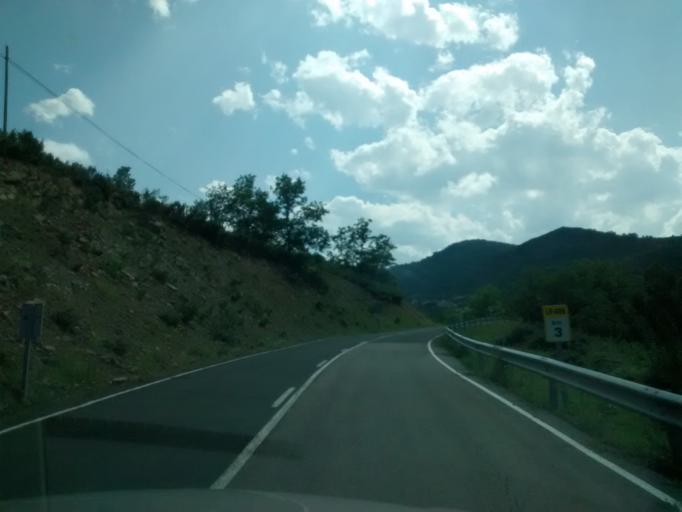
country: ES
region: La Rioja
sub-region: Provincia de La Rioja
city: Rabanera
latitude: 42.1964
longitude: -2.4792
